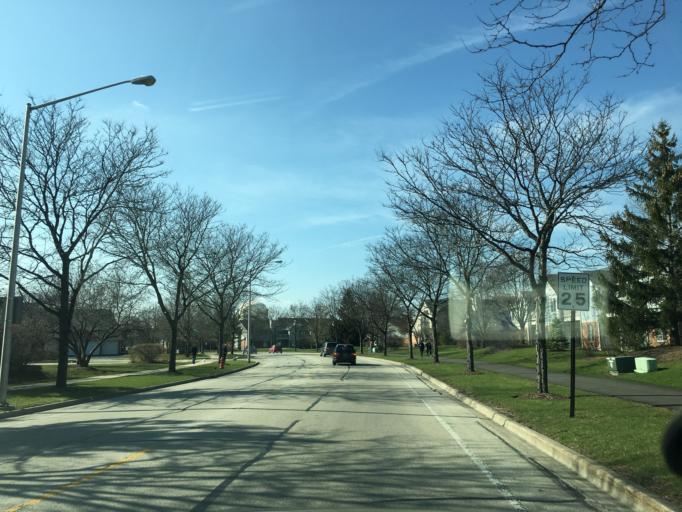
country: US
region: Illinois
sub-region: DuPage County
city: Hanover Park
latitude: 42.0197
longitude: -88.1417
